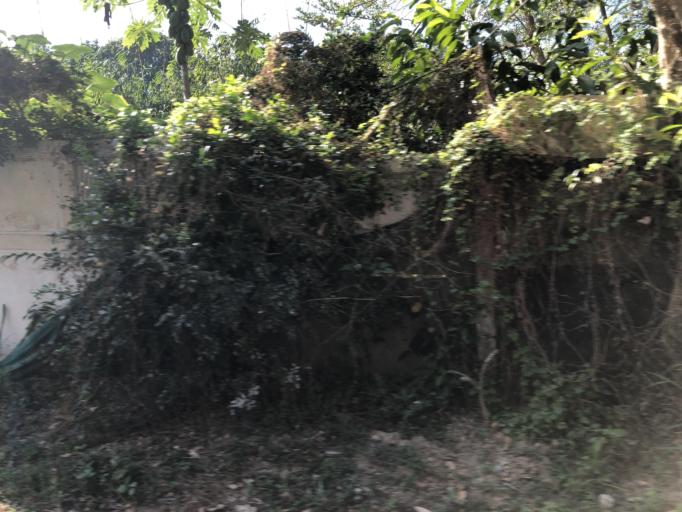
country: TW
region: Taiwan
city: Yujing
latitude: 23.0123
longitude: 120.3857
